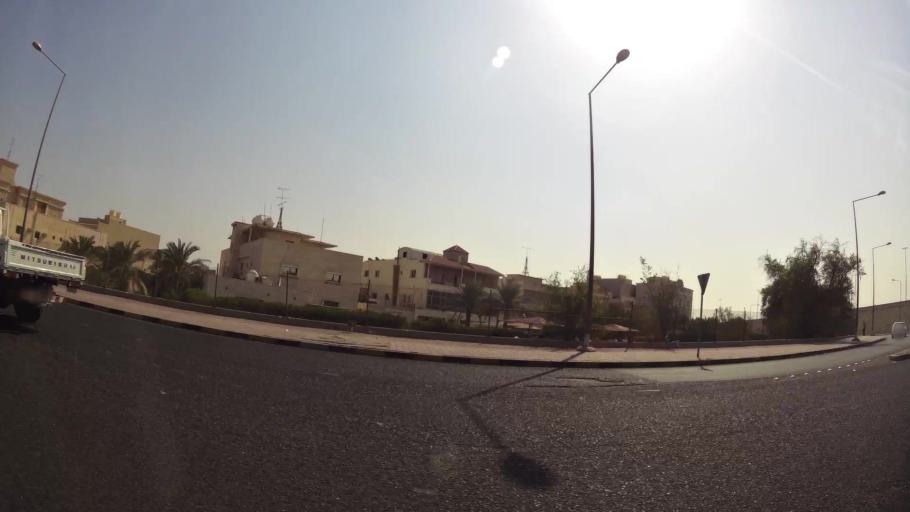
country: KW
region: Al Ahmadi
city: Al Fahahil
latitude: 29.0907
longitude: 48.1170
